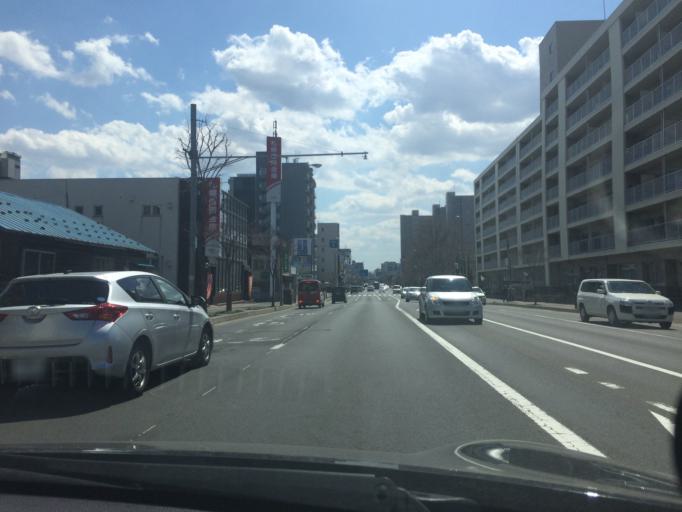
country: JP
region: Hokkaido
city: Sapporo
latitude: 43.0746
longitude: 141.3647
